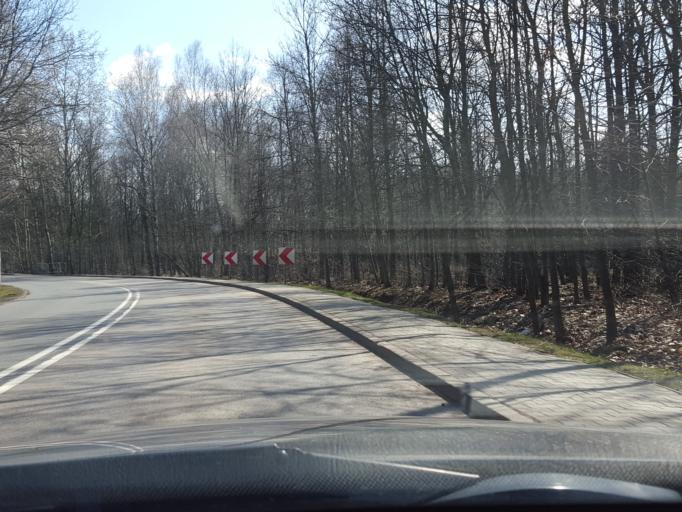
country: PL
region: Silesian Voivodeship
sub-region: Ruda Slaska
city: Ruda Slaska
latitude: 50.2352
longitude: 18.8568
